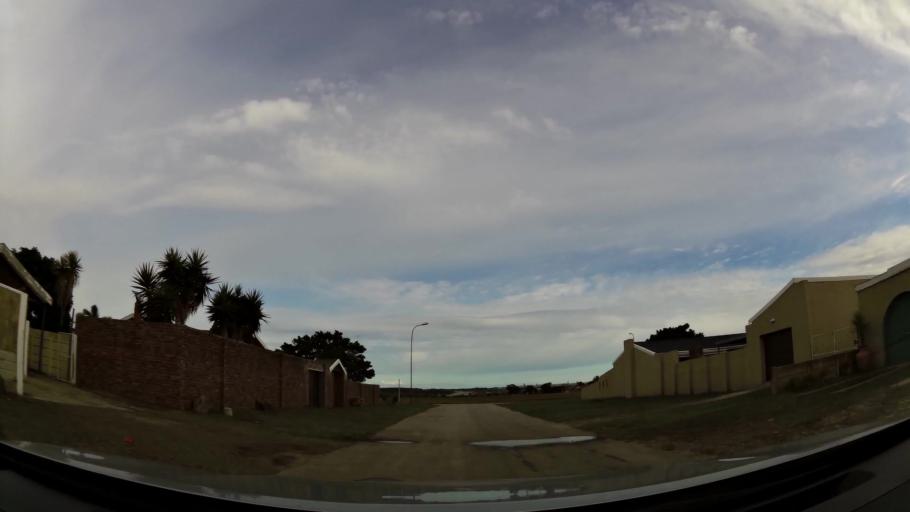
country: ZA
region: Eastern Cape
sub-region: Nelson Mandela Bay Metropolitan Municipality
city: Port Elizabeth
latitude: -33.9361
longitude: 25.4681
